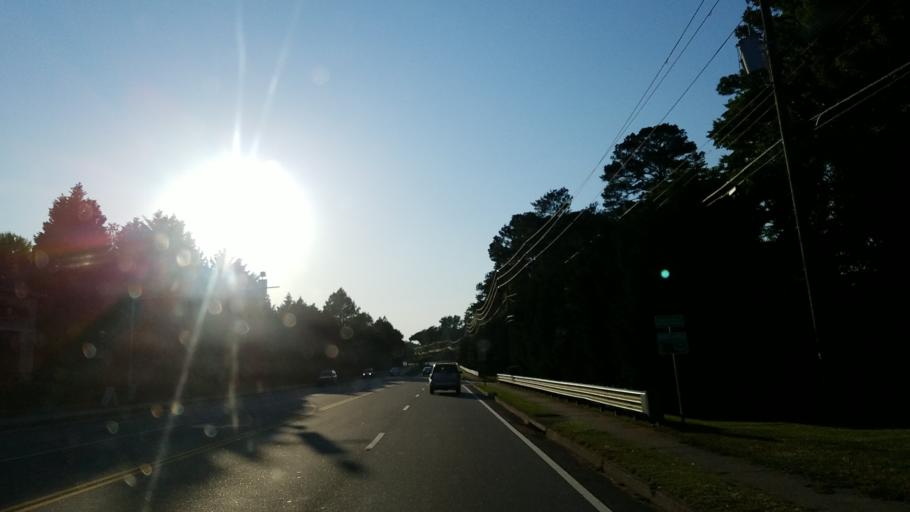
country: US
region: Georgia
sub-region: Cobb County
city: Smyrna
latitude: 33.8742
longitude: -84.5012
